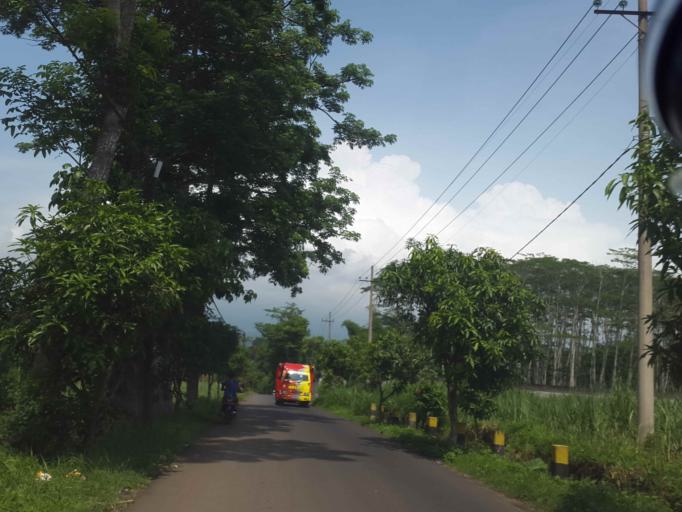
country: ID
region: East Java
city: Lawang
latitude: -7.8560
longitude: 112.7082
